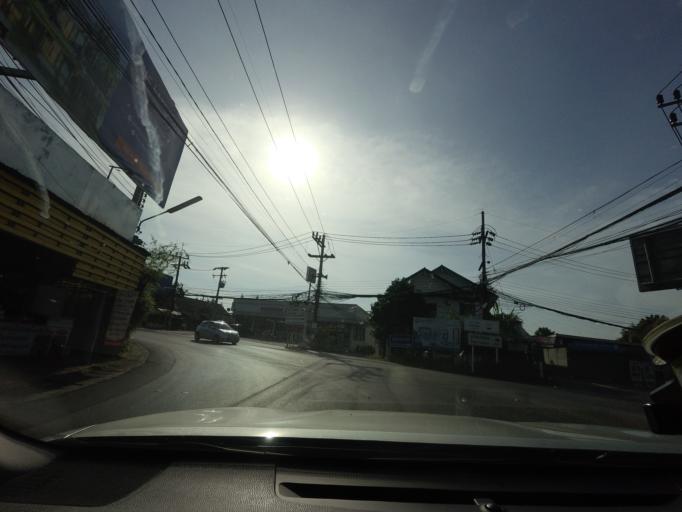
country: TH
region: Phuket
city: Thalang
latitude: 8.0162
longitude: 98.3183
